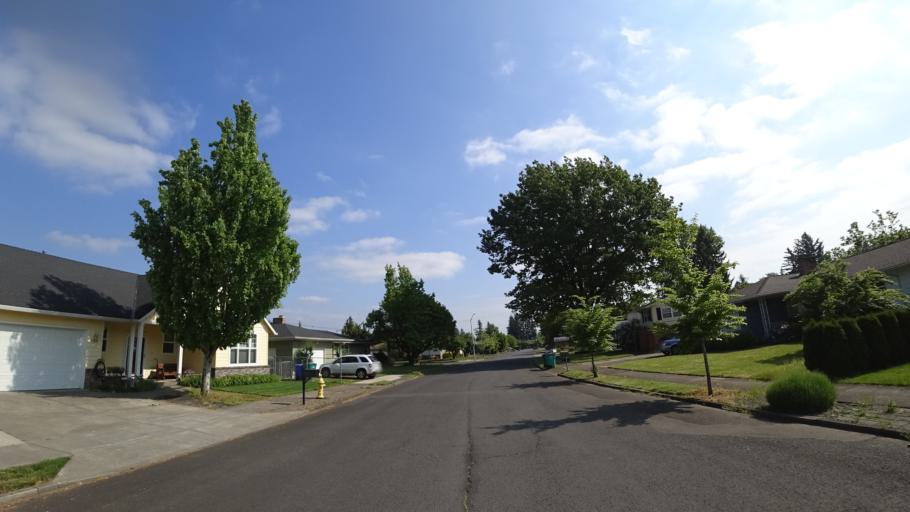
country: US
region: Oregon
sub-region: Multnomah County
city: Fairview
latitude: 45.5177
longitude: -122.4919
